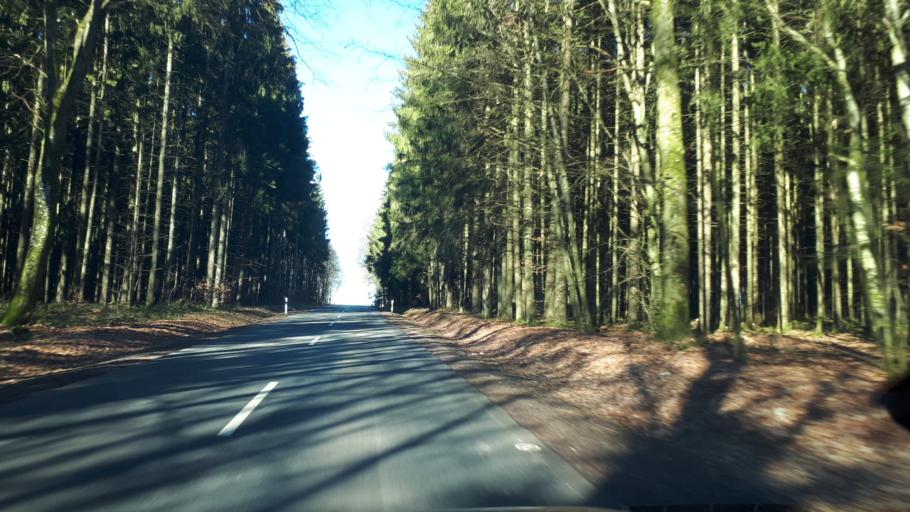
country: DE
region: Rheinland-Pfalz
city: Muckeln
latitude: 50.0986
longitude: 6.9152
